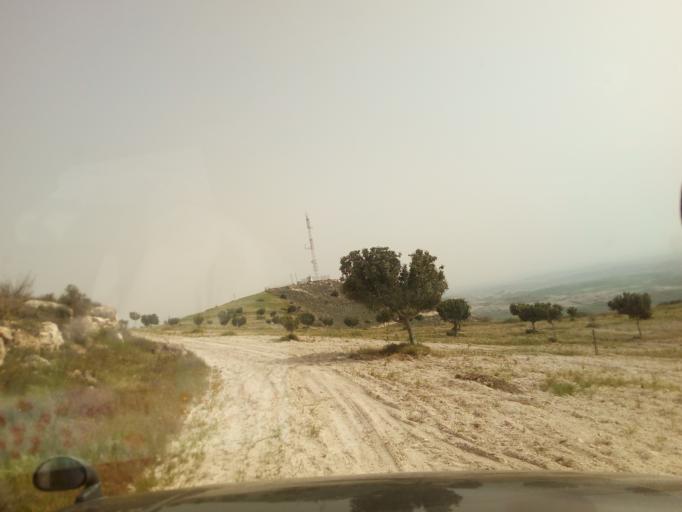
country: CY
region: Larnaka
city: Athienou
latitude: 35.0119
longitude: 33.5378
